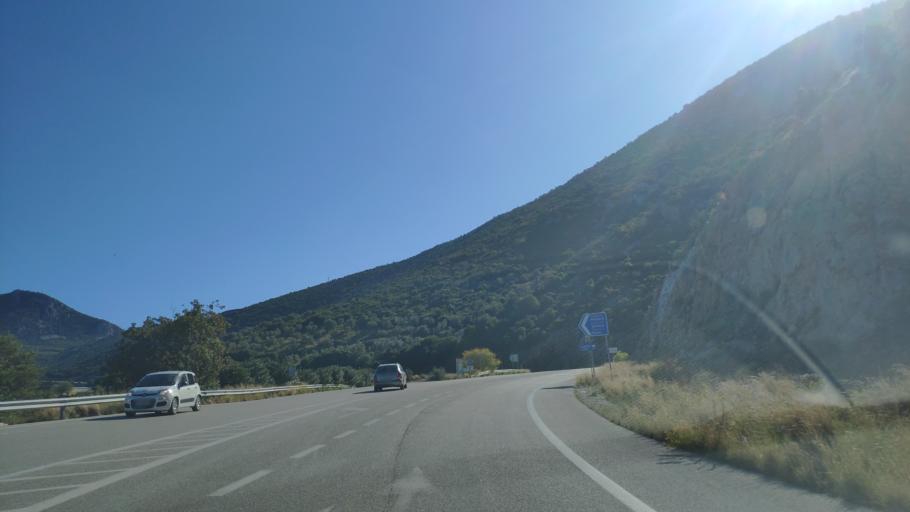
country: GR
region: Peloponnese
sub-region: Nomos Argolidos
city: Palaia Epidavros
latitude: 37.6125
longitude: 23.1519
